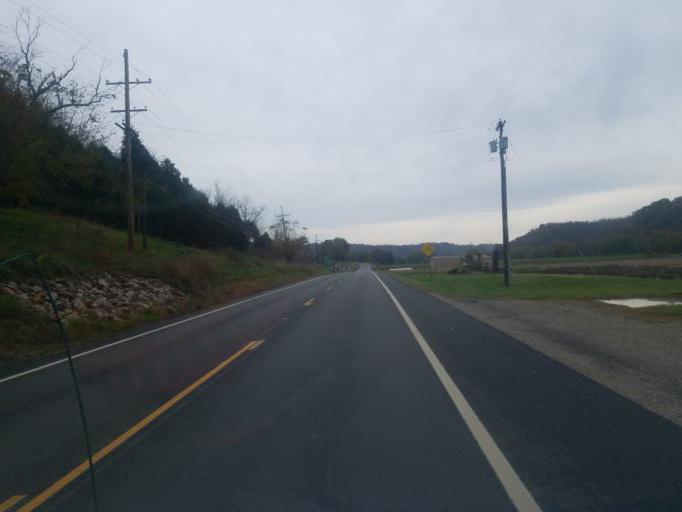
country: US
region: Ohio
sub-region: Washington County
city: Devola
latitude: 39.5252
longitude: -81.4985
